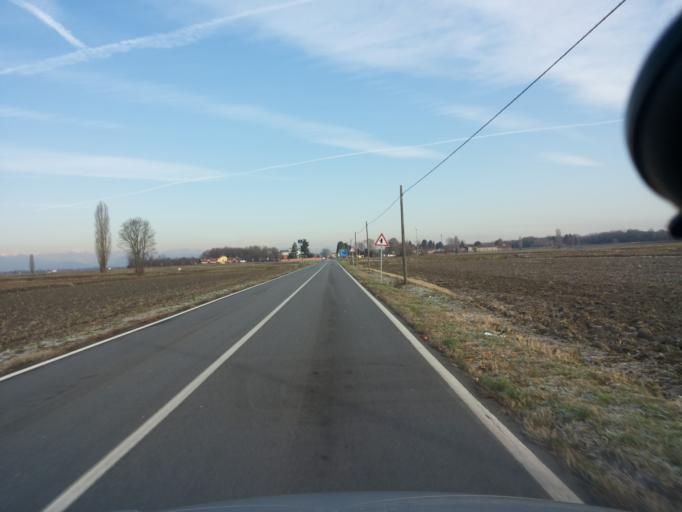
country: IT
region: Piedmont
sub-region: Provincia di Vercelli
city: Albano Vercellese
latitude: 45.4168
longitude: 8.3791
